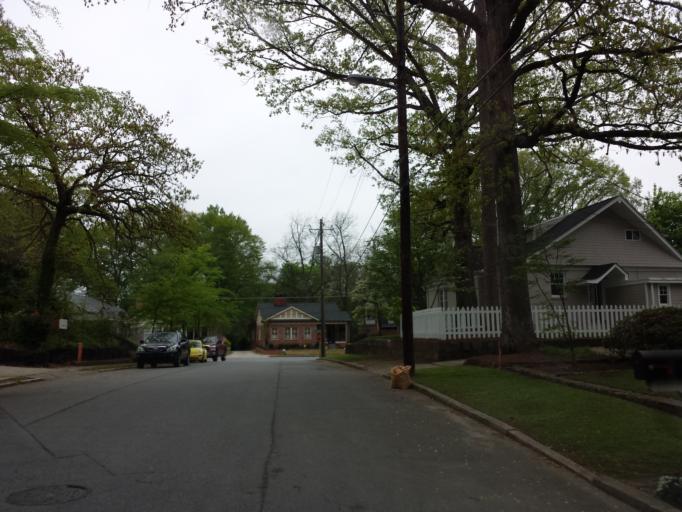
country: US
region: Georgia
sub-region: DeKalb County
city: Druid Hills
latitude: 33.7921
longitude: -84.3551
